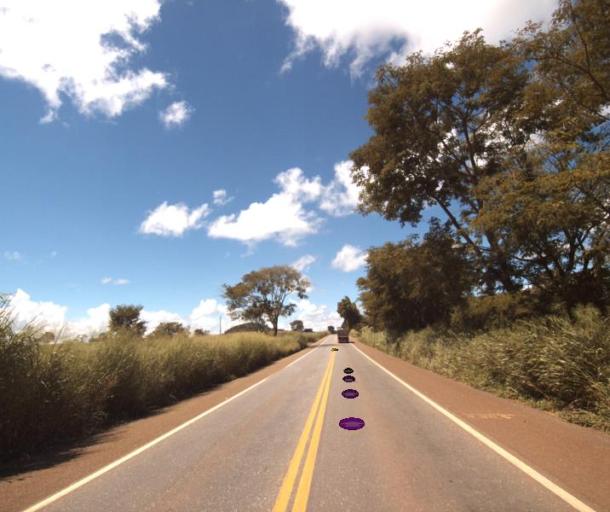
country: BR
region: Goias
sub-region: Pirenopolis
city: Pirenopolis
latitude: -16.0379
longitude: -49.0819
